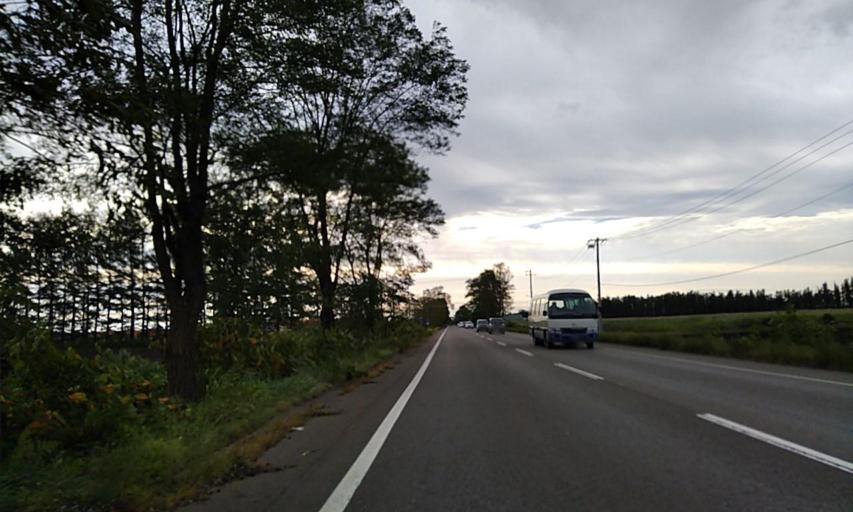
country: JP
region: Hokkaido
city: Obihiro
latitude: 42.9244
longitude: 142.9895
